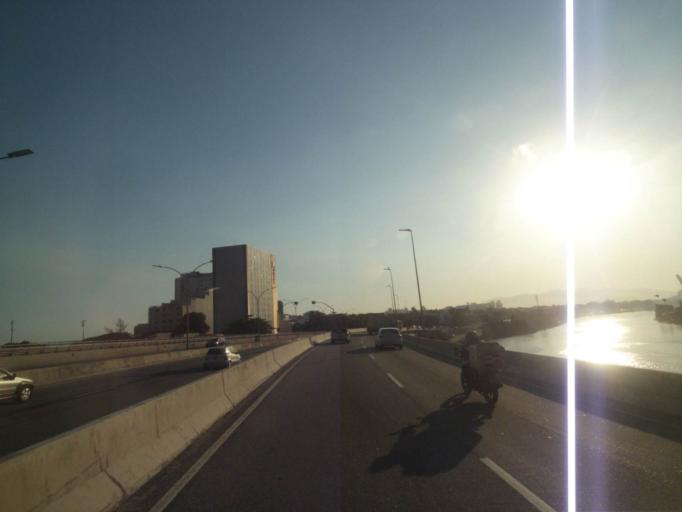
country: BR
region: Rio de Janeiro
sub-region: Rio De Janeiro
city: Rio de Janeiro
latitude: -23.0129
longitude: -43.2964
